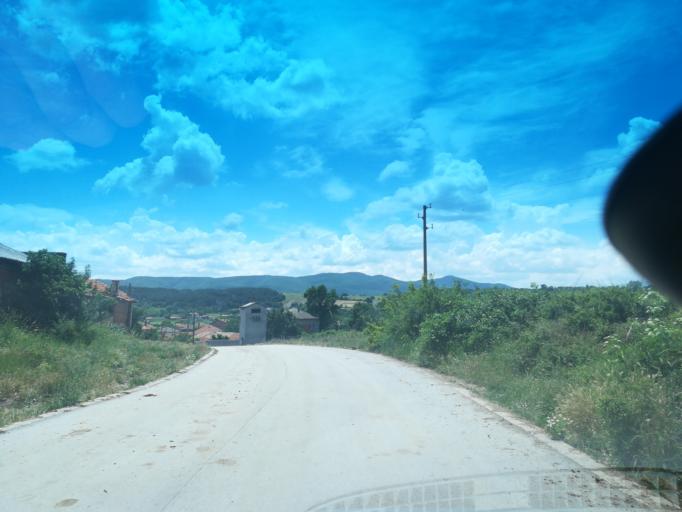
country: BG
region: Khaskovo
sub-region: Obshtina Mineralni Bani
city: Mineralni Bani
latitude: 41.9501
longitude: 25.2475
